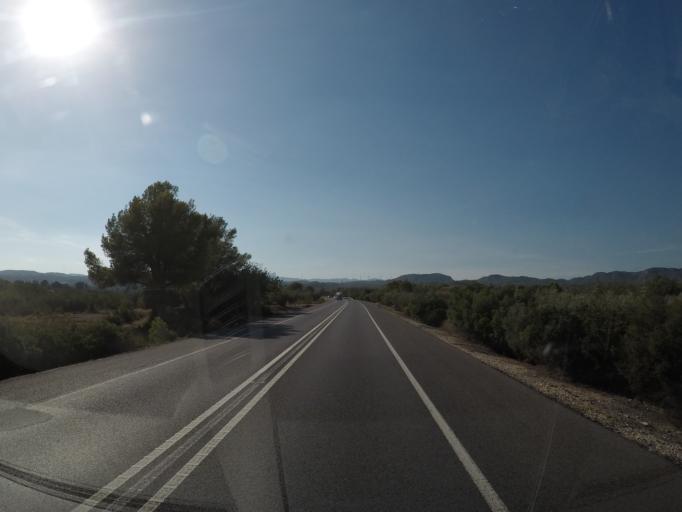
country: ES
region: Catalonia
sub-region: Provincia de Tarragona
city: El Perello
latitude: 40.8974
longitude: 0.7382
